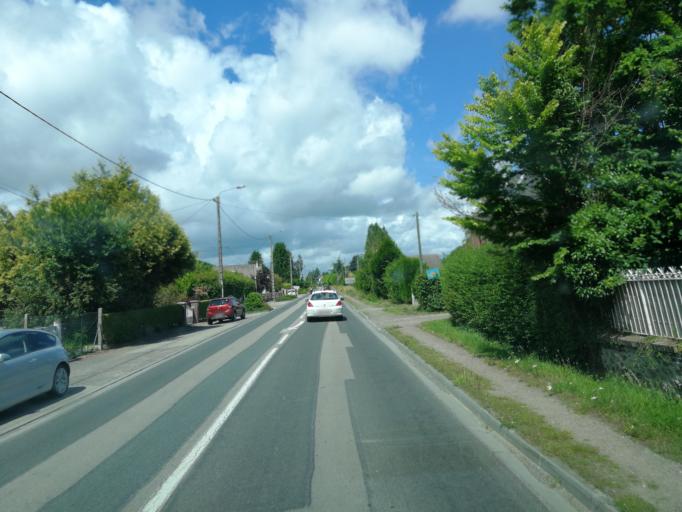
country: FR
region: Haute-Normandie
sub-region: Departement de l'Eure
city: Saint-Ouen-de-Thouberville
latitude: 49.3569
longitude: 0.8831
